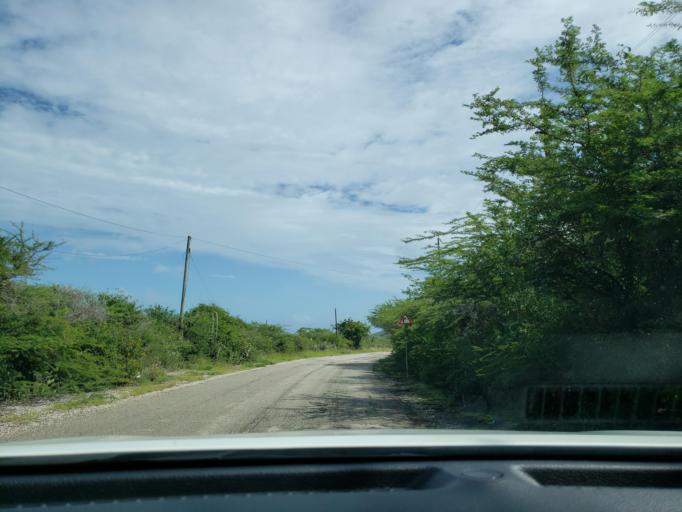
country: CW
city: Barber
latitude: 12.3155
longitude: -69.0883
